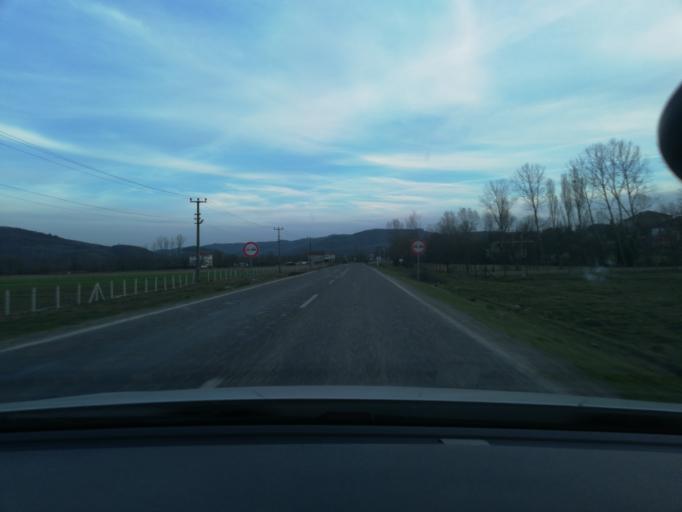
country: TR
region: Zonguldak
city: Saltukova
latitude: 41.5160
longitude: 32.1028
